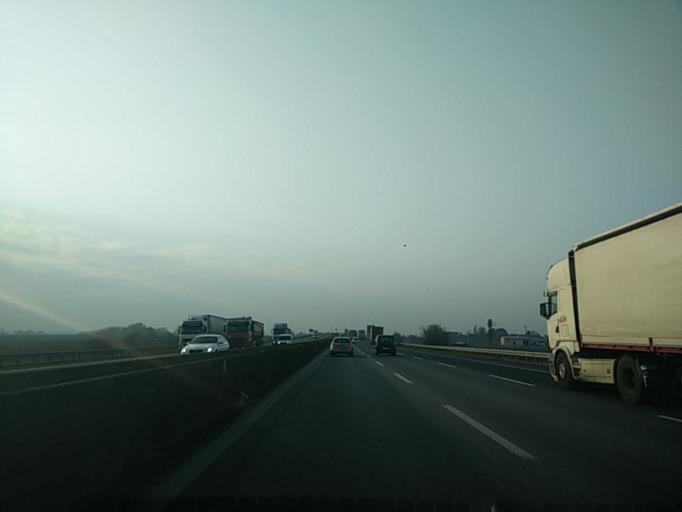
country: IT
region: Emilia-Romagna
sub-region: Provincia di Ravenna
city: Solarolo
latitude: 44.3484
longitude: 11.8336
